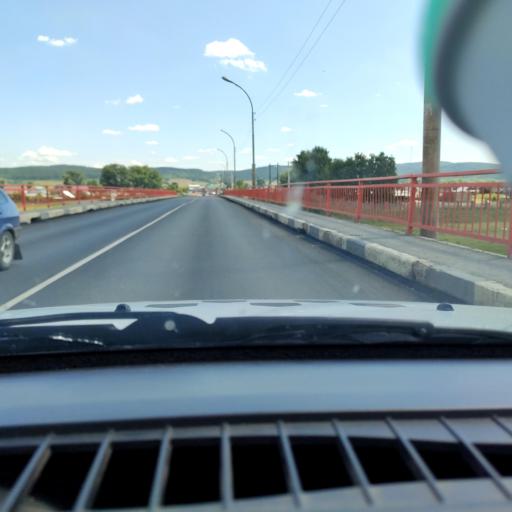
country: RU
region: Bashkortostan
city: Mesyagutovo
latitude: 55.5312
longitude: 58.2527
